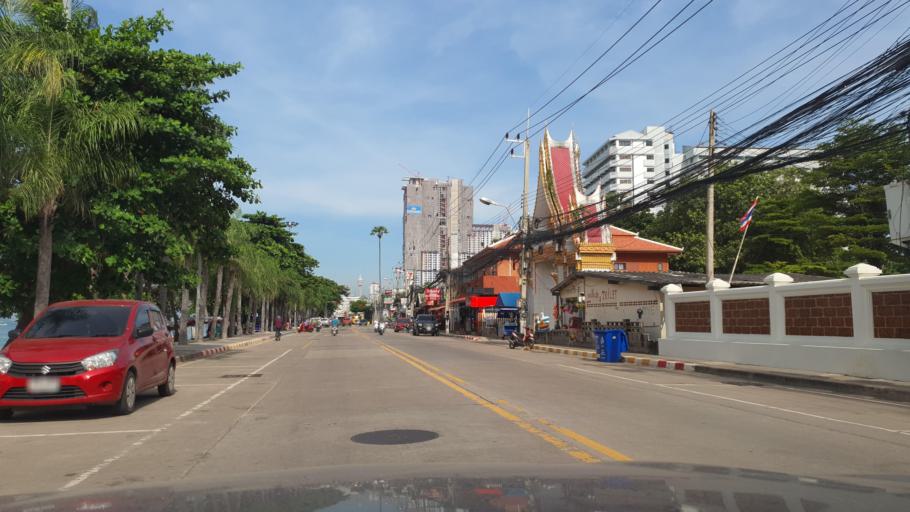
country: TH
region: Chon Buri
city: Phatthaya
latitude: 12.8844
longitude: 100.8795
